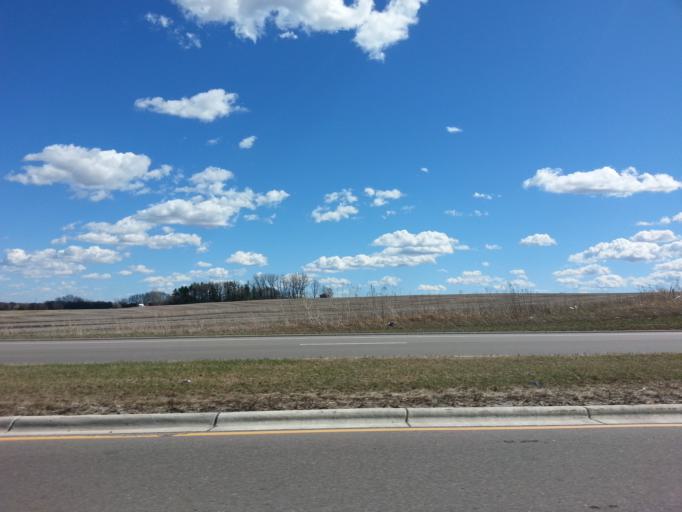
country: US
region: Minnesota
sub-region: Dakota County
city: Lakeville
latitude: 44.6876
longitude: -93.2427
